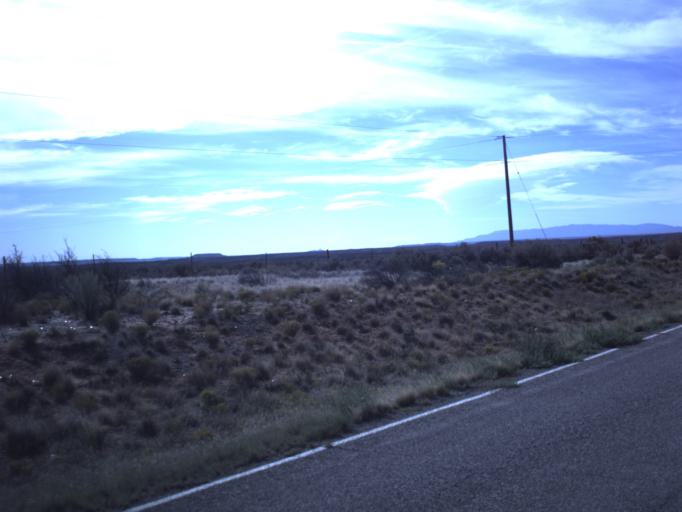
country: US
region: Utah
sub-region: San Juan County
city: Blanding
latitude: 37.3947
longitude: -109.3387
